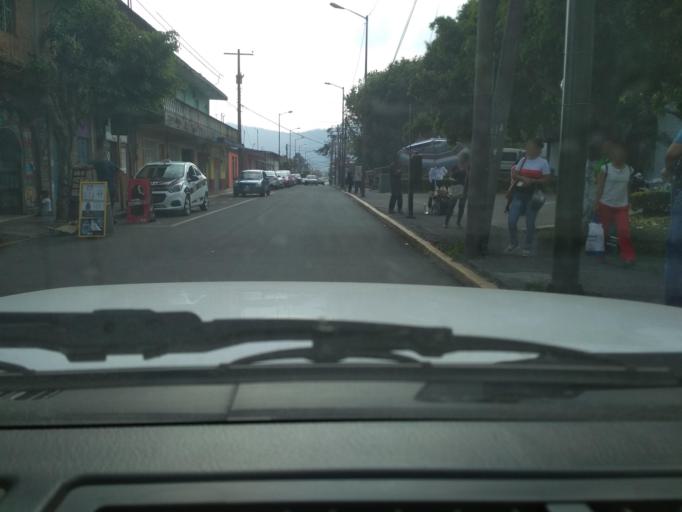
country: MX
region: Veracruz
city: Orizaba
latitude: 18.8687
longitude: -97.0959
